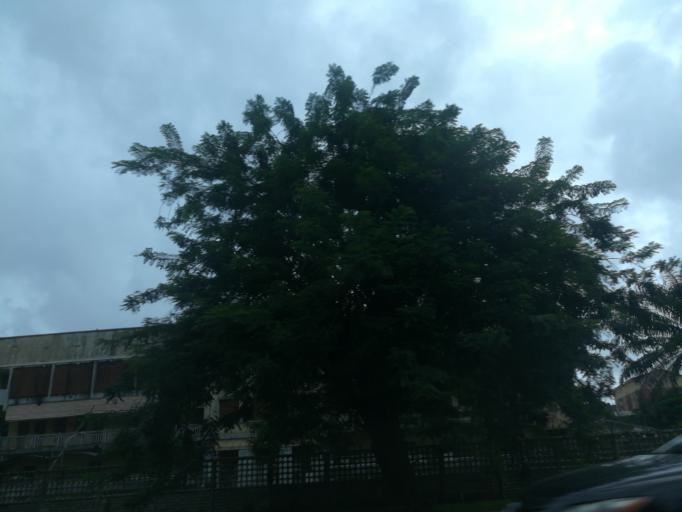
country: NG
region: Lagos
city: Ikoyi
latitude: 6.4555
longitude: 3.4462
